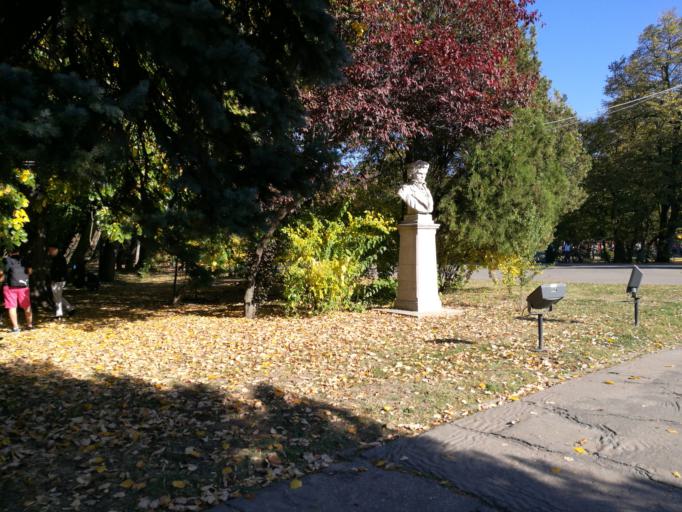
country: RO
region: Bucuresti
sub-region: Municipiul Bucuresti
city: Bucuresti
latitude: 44.4704
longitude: 26.0833
